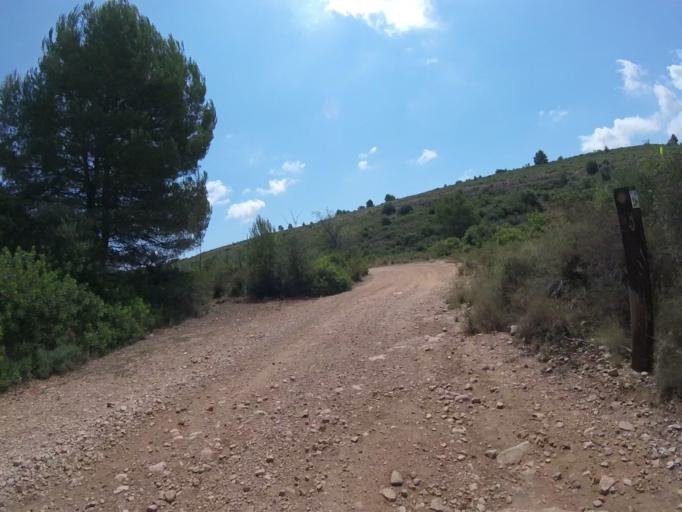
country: ES
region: Valencia
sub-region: Provincia de Castello
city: Torreblanca
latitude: 40.2133
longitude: 0.1453
